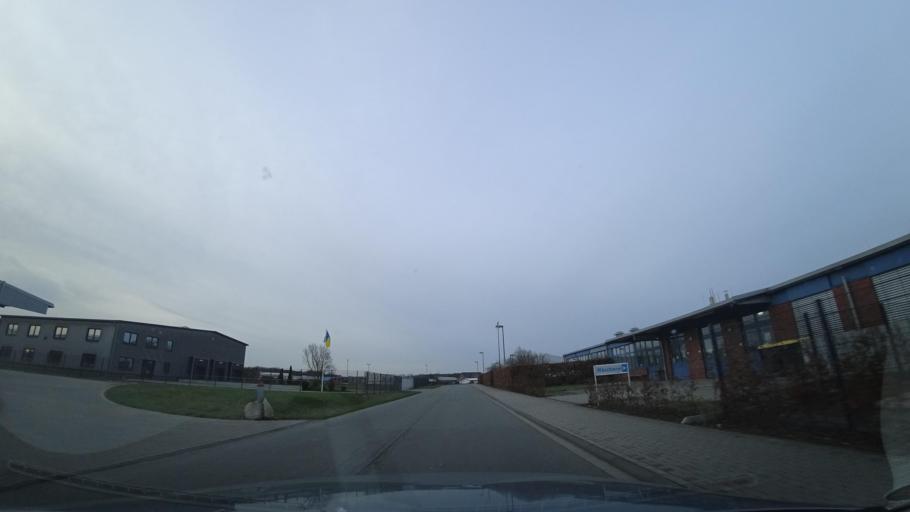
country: DE
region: Lower Saxony
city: Wardenburg
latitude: 53.0579
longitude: 8.2403
